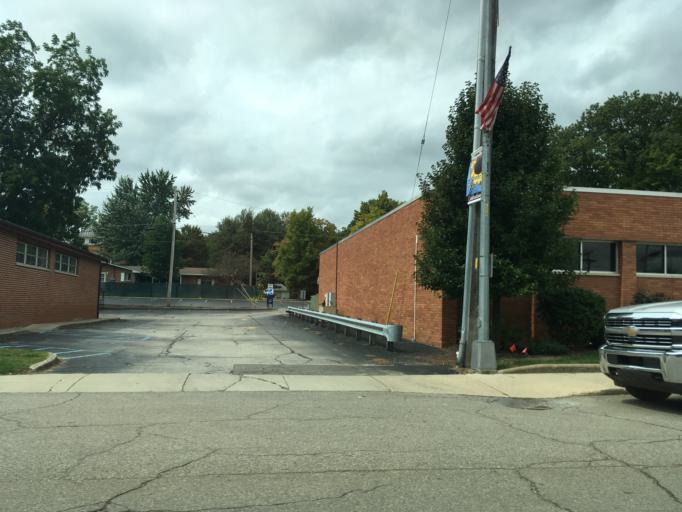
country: US
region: Michigan
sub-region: Lapeer County
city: Barnes Lake-Millers Lake
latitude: 43.3348
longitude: -83.3526
